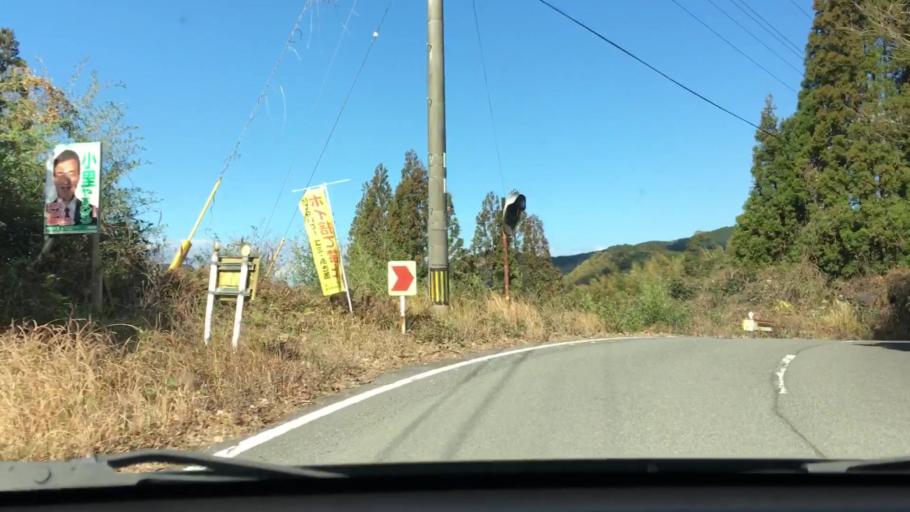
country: JP
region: Kagoshima
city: Ijuin
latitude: 31.7275
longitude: 130.4182
